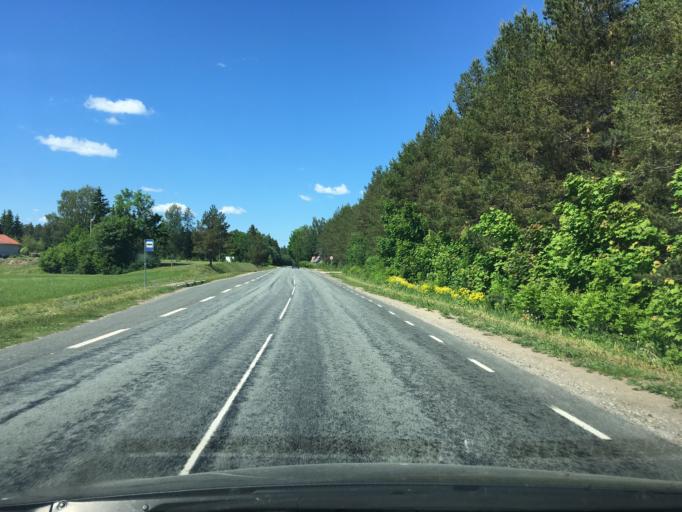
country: EE
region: Harju
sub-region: Rae vald
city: Vaida
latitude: 59.2034
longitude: 24.9532
